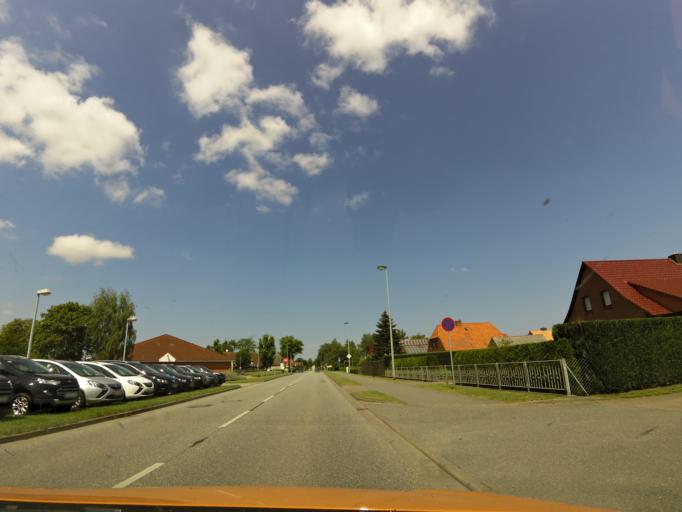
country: DE
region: Mecklenburg-Vorpommern
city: Rehna
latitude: 53.7734
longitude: 11.0518
